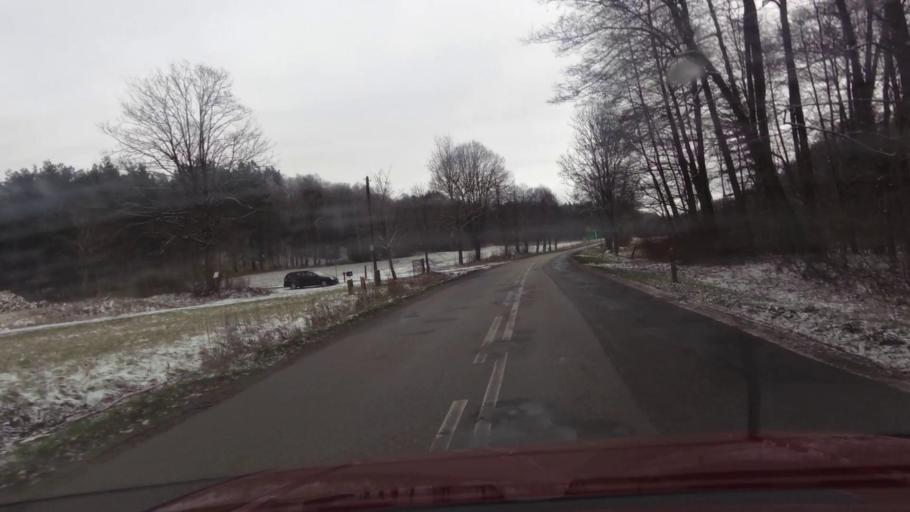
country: PL
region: West Pomeranian Voivodeship
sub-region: Powiat swidwinski
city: Polczyn-Zdroj
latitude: 53.7949
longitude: 16.0617
